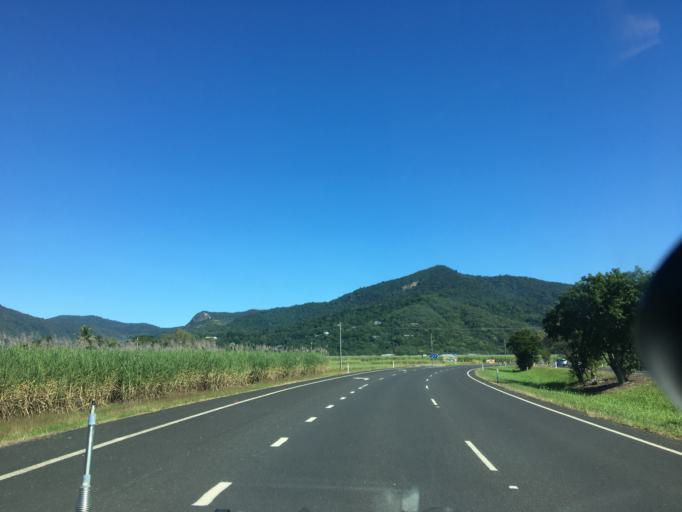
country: AU
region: Queensland
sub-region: Cairns
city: Redlynch
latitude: -16.8507
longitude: 145.7074
